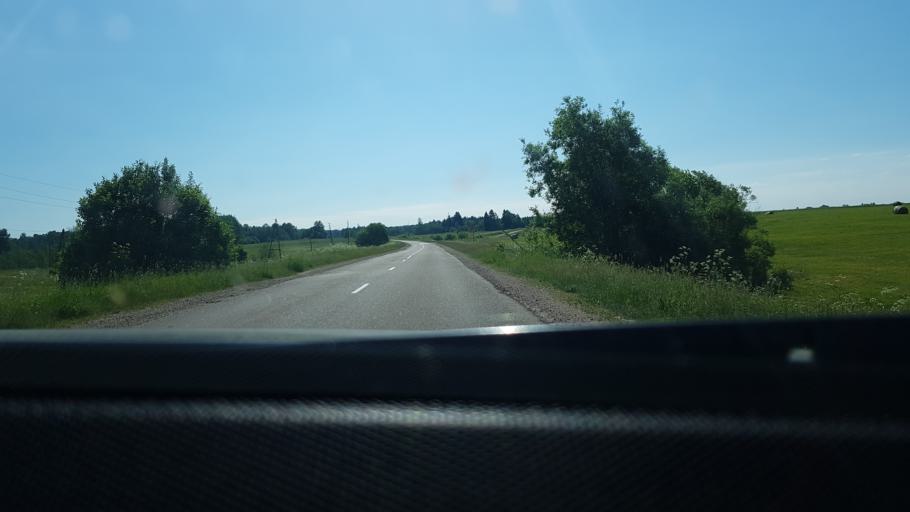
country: LV
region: Daugavpils
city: Daugavpils
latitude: 55.8184
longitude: 26.8033
